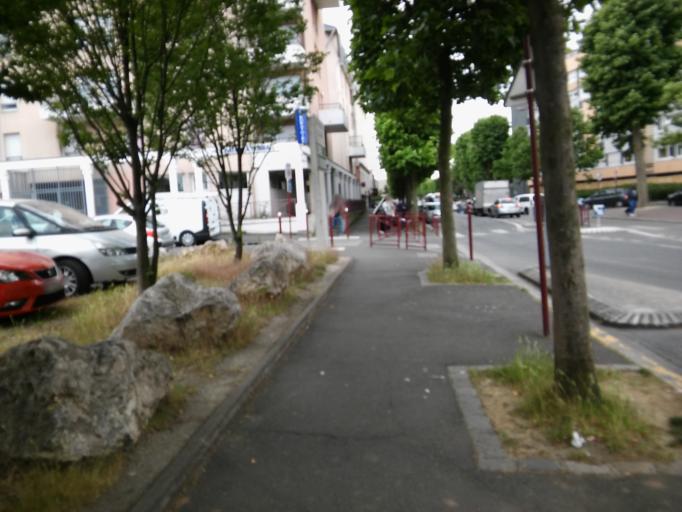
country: FR
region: Ile-de-France
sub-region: Departement de Seine-Saint-Denis
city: Bondy
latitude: 48.9133
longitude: 2.4823
